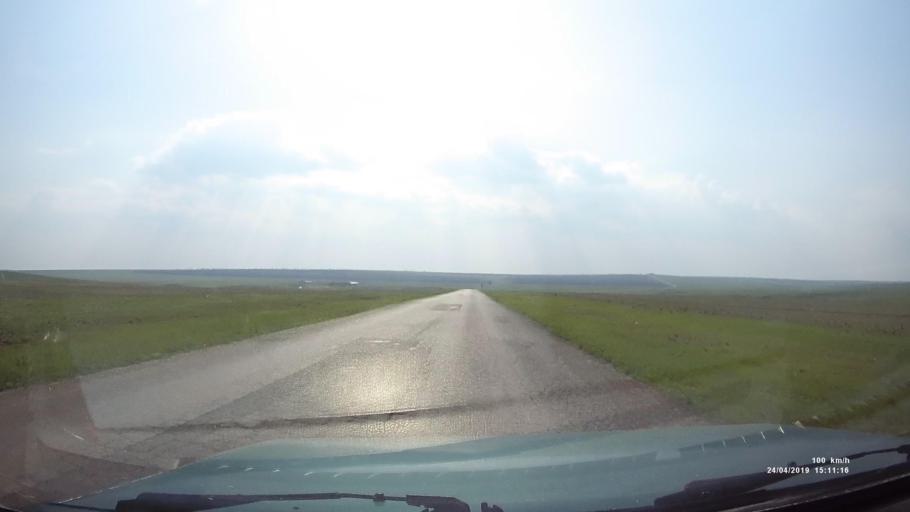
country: RU
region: Rostov
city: Remontnoye
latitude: 46.5451
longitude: 43.3245
